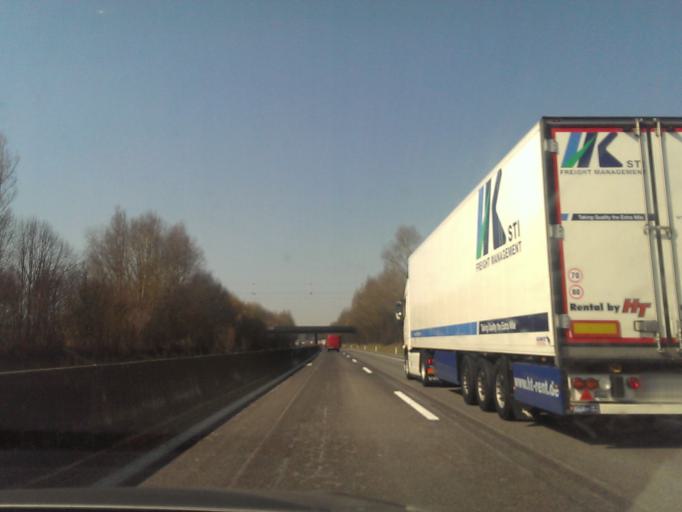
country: AT
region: Upper Austria
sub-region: Politischer Bezirk Ried im Innkreis
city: Ried im Innkreis
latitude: 48.2264
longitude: 13.6052
